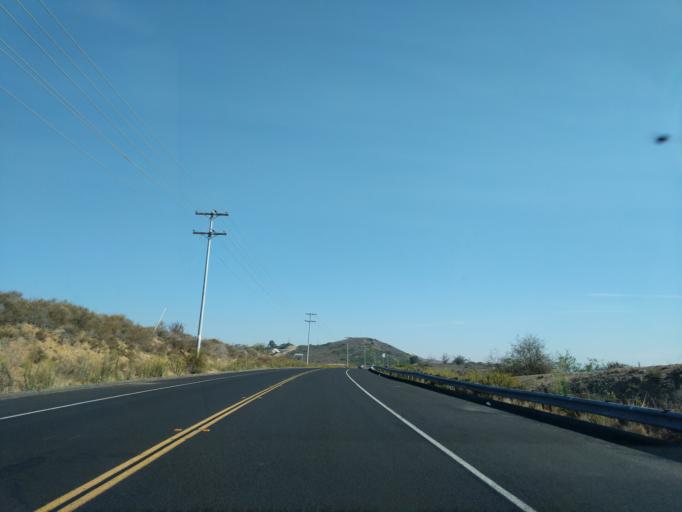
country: US
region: California
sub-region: Orange County
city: San Clemente
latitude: 33.3982
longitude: -117.5912
